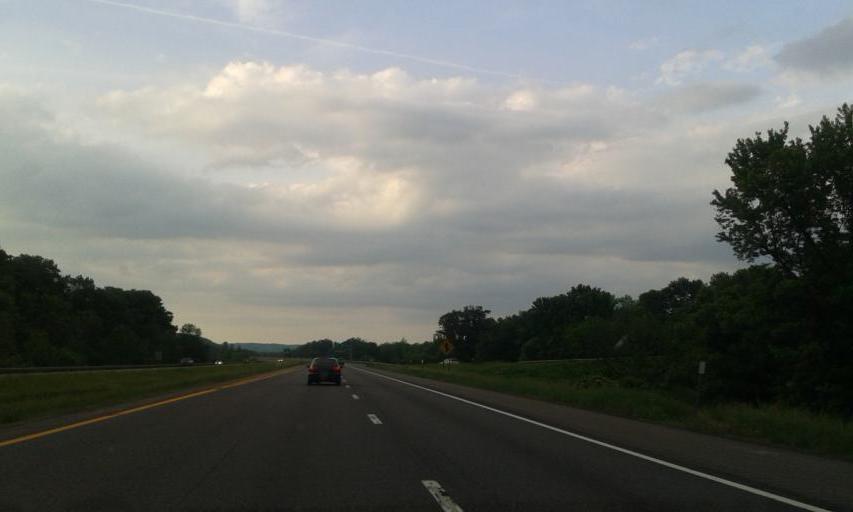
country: US
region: New York
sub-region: Broome County
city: Port Dickinson
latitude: 42.1429
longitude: -75.9004
